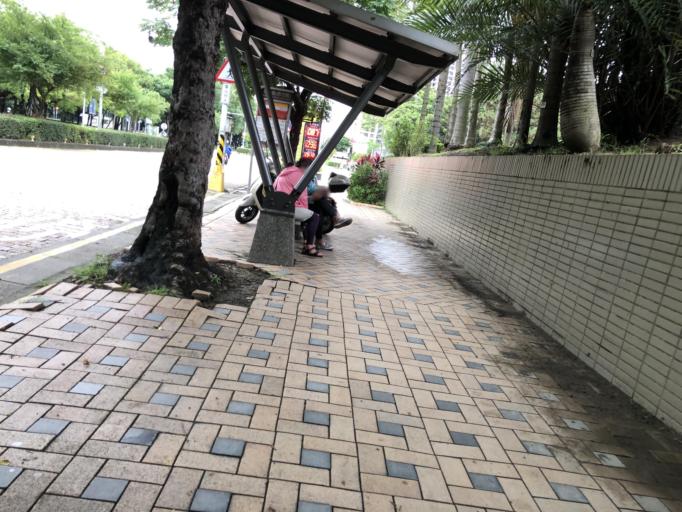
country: TW
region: Taiwan
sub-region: Taichung City
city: Taichung
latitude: 24.1584
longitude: 120.6667
